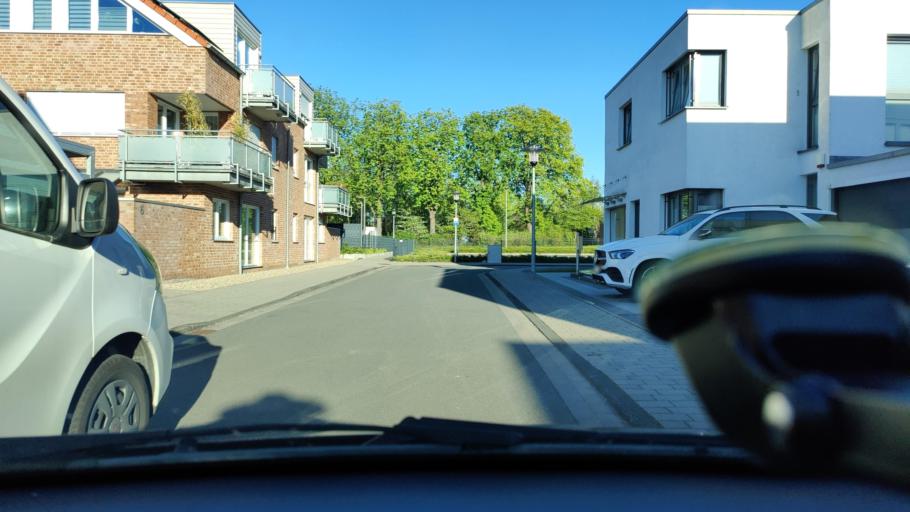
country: DE
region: North Rhine-Westphalia
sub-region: Regierungsbezirk Munster
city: Ahaus
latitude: 52.0776
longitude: 7.0145
